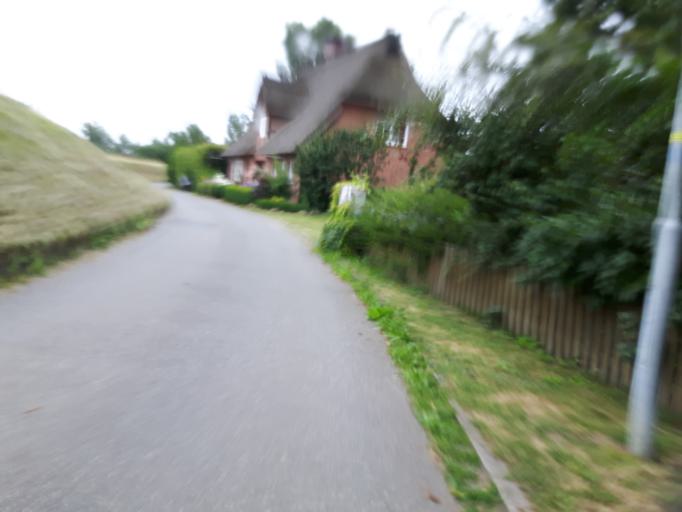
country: DE
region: Lower Saxony
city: Winsen
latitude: 53.3772
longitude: 10.2016
